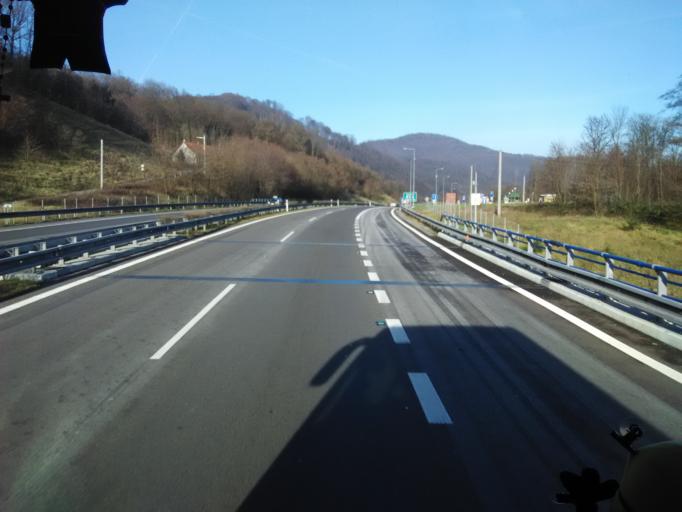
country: SK
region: Banskobystricky
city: Zarnovica
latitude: 48.4607
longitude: 18.6906
